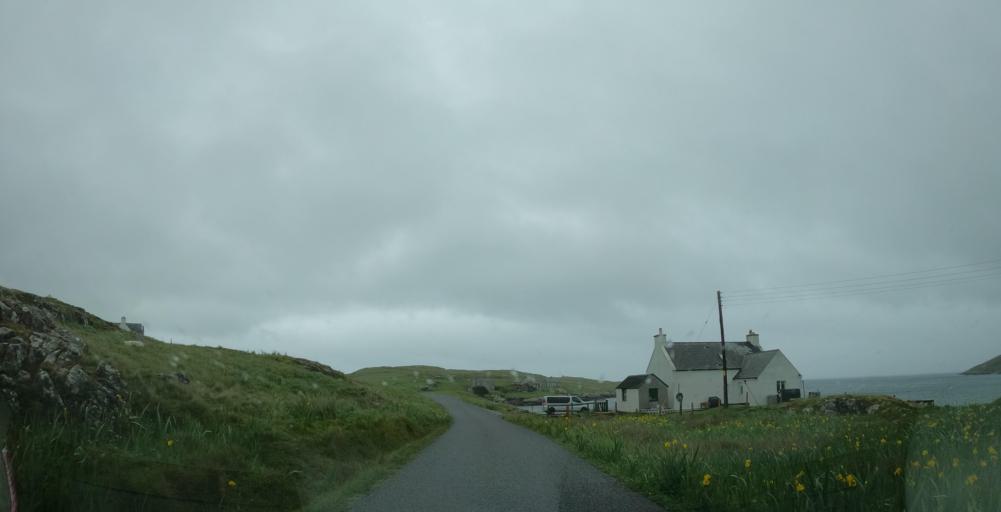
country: GB
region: Scotland
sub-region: Eilean Siar
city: Barra
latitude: 56.9637
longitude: -7.4400
